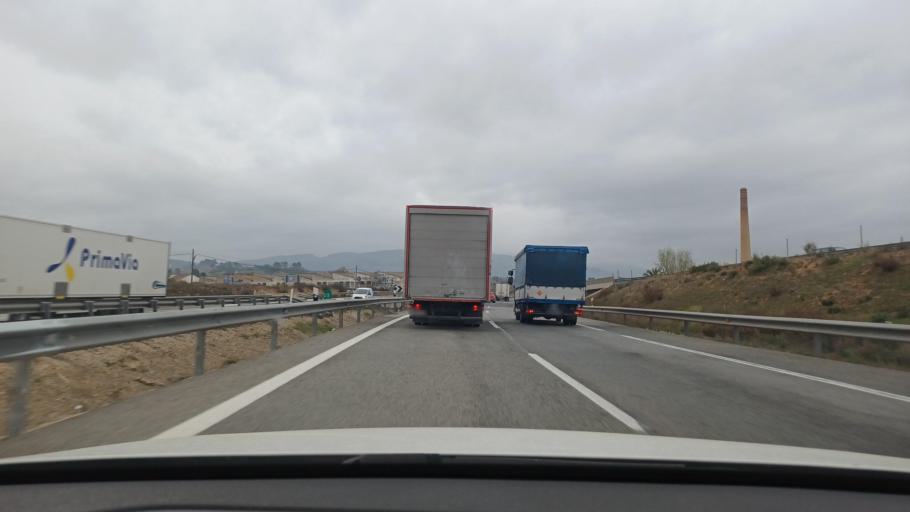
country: ES
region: Valencia
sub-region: Provincia de Alicante
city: Sax
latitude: 38.5478
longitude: -0.8156
